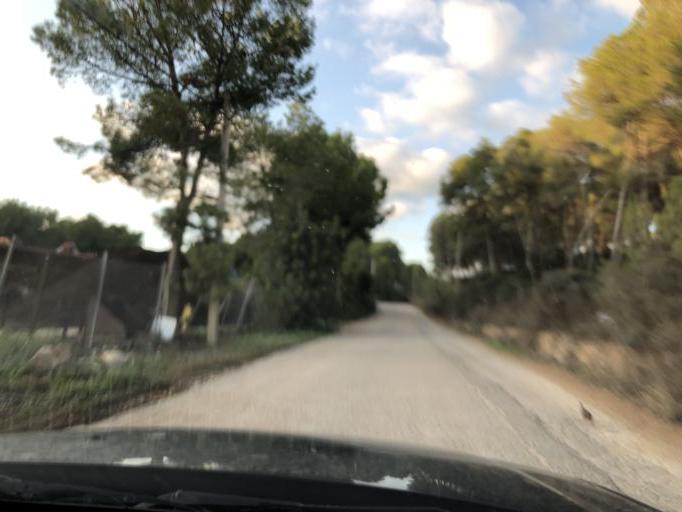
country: ES
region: Balearic Islands
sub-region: Illes Balears
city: Santa Ponsa
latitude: 39.5394
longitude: 2.4840
